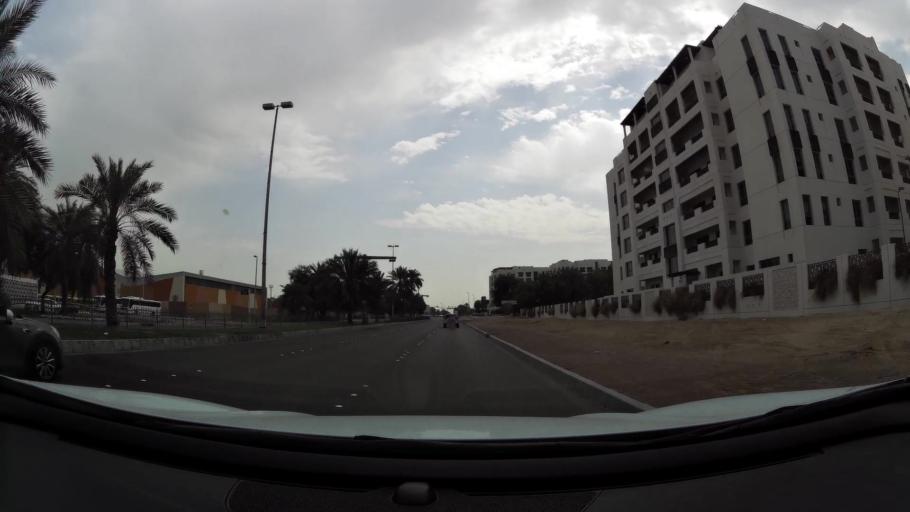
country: AE
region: Abu Dhabi
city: Abu Dhabi
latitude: 24.4586
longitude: 54.3533
